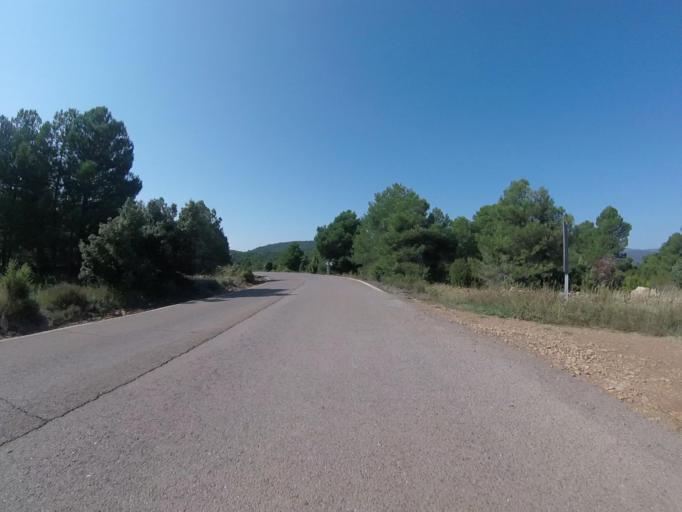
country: ES
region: Valencia
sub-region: Provincia de Castello
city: Benafigos
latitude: 40.2875
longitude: -0.2383
